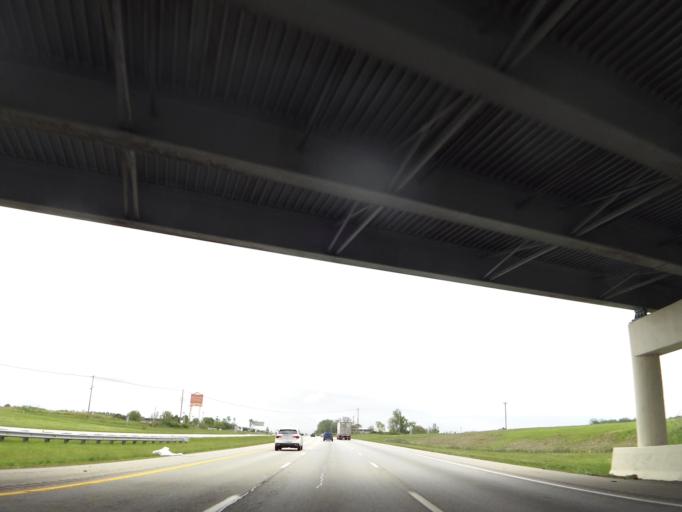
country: US
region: Ohio
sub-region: Fayette County
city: Jeffersonville
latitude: 39.6489
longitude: -83.5404
